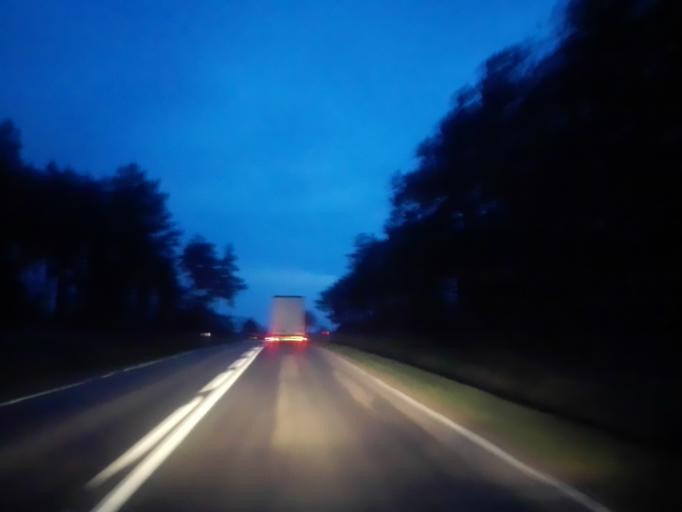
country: PL
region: Podlasie
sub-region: Powiat lomzynski
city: Sniadowo
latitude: 53.0660
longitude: 22.0070
